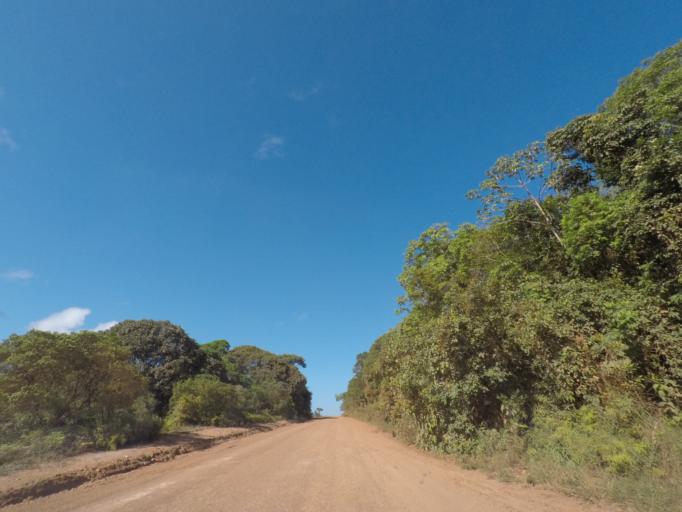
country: BR
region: Bahia
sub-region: Marau
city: Marau
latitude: -14.1156
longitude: -38.9861
